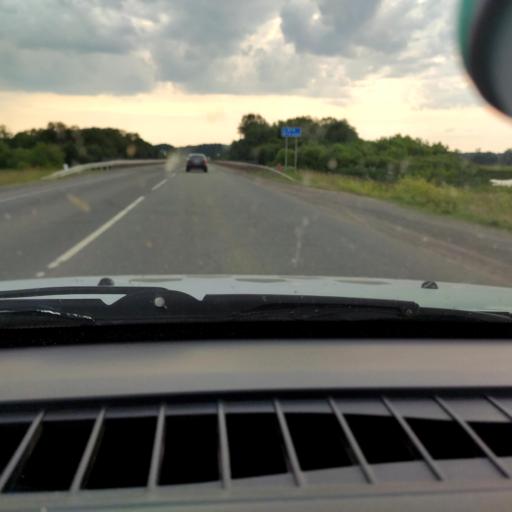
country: RU
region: Udmurtiya
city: Igra
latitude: 57.6228
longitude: 53.3835
